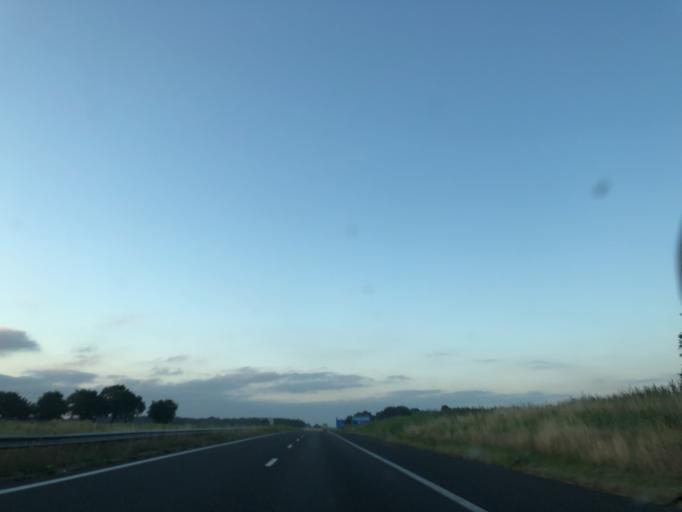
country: NL
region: Groningen
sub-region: Gemeente  Oldambt
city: Winschoten
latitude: 53.1807
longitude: 6.9841
